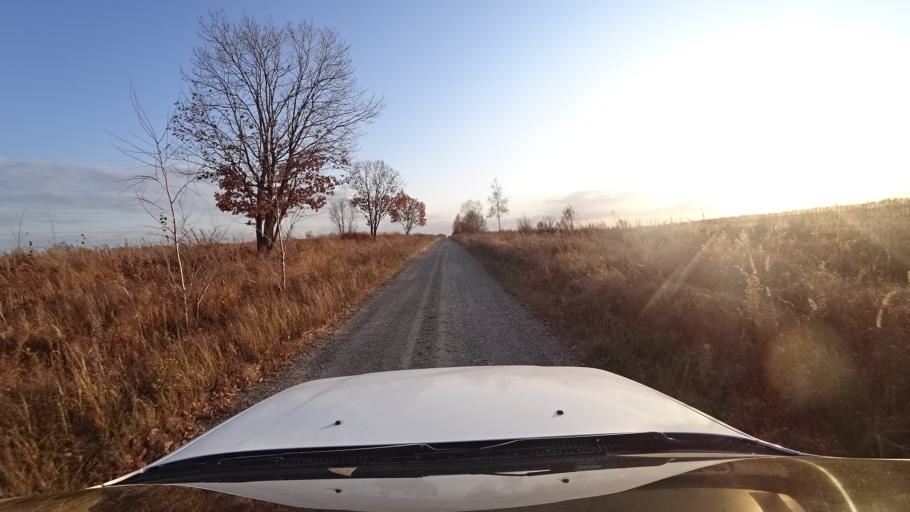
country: RU
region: Primorskiy
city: Lazo
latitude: 45.8133
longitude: 133.6095
